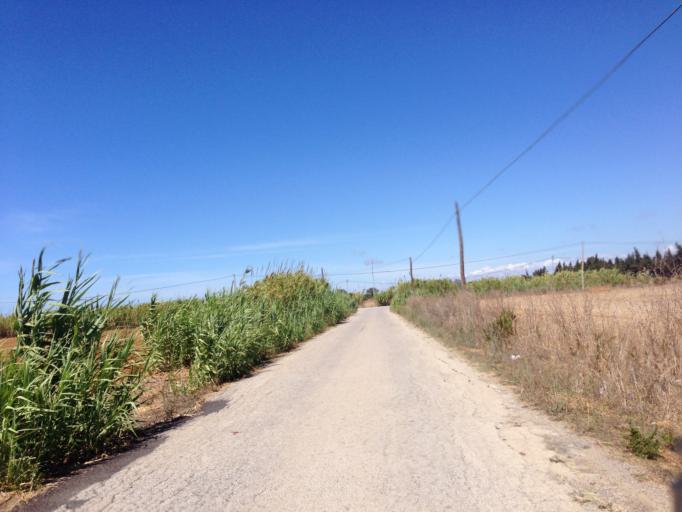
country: ES
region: Andalusia
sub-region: Provincia de Cadiz
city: Conil de la Frontera
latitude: 36.3361
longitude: -6.1278
